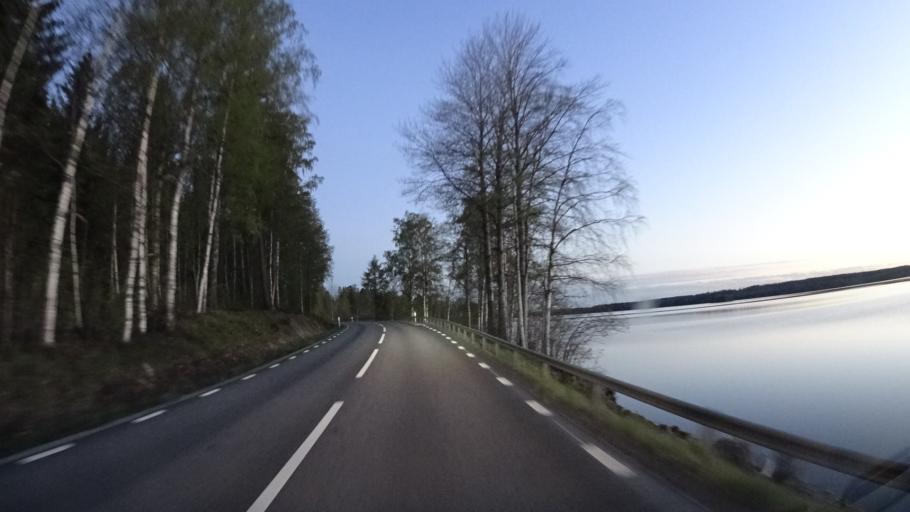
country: SE
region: OErebro
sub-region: Nora Kommun
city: As
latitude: 59.4922
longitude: 14.9430
